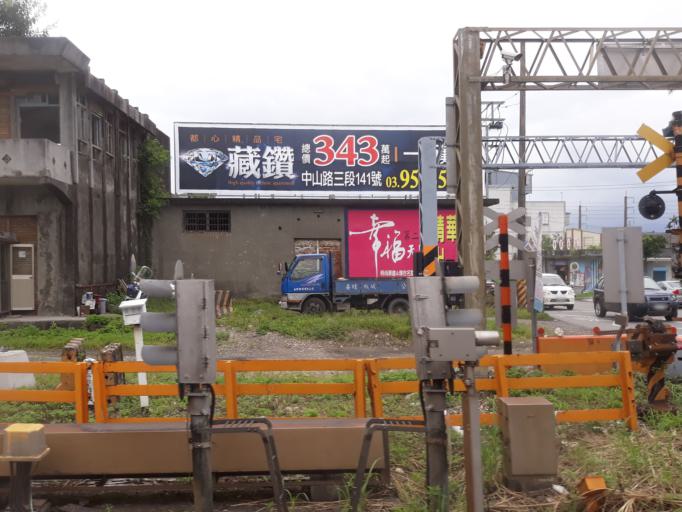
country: TW
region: Taiwan
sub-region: Yilan
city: Yilan
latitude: 24.6928
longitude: 121.7751
